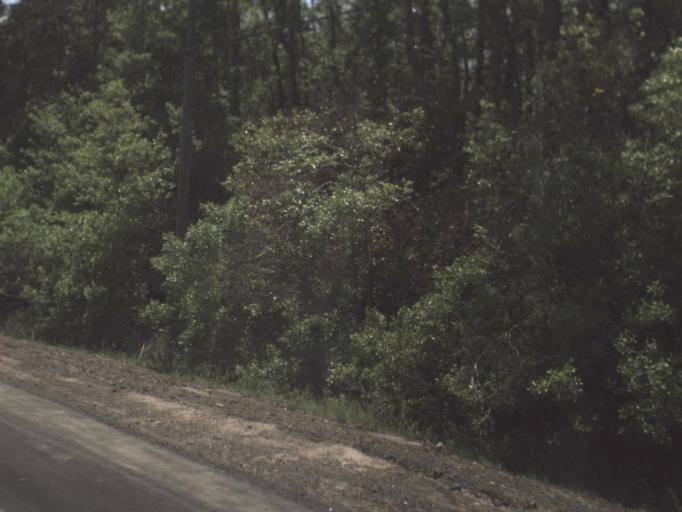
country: US
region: Florida
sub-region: Escambia County
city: Myrtle Grove
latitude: 30.3901
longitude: -87.3092
